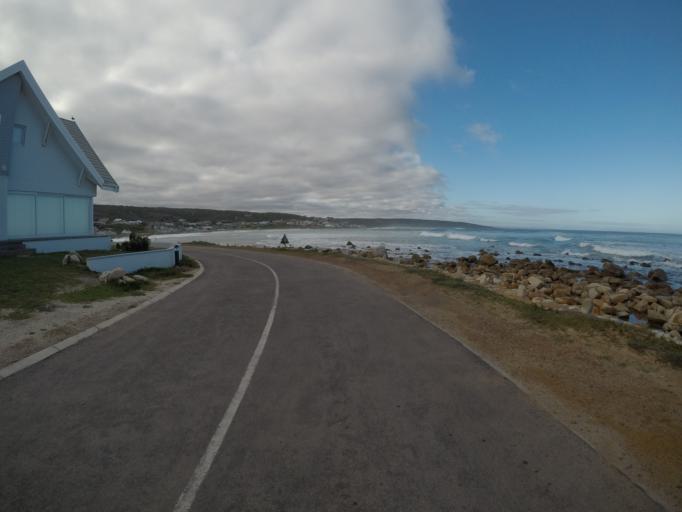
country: ZA
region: Western Cape
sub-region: Eden District Municipality
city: Riversdale
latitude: -34.4324
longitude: 21.3357
